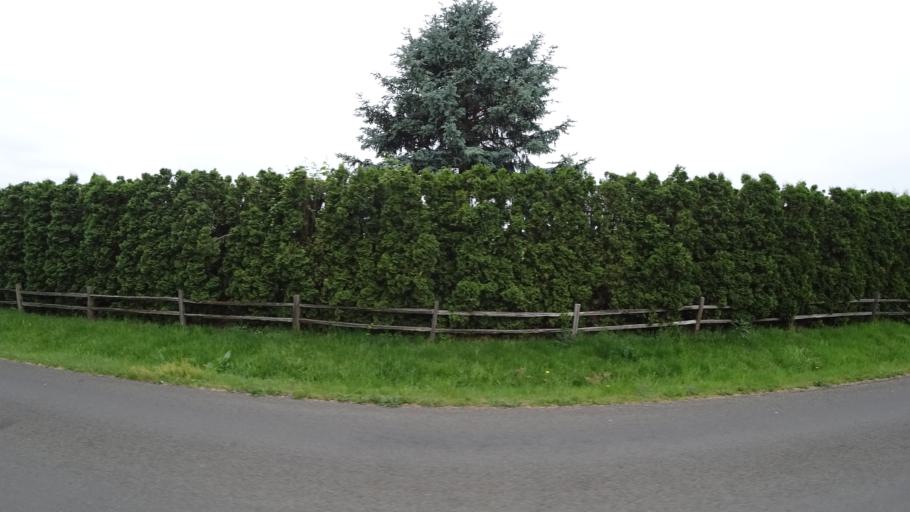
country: US
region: Oregon
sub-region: Washington County
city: Aloha
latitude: 45.4828
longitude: -122.9137
